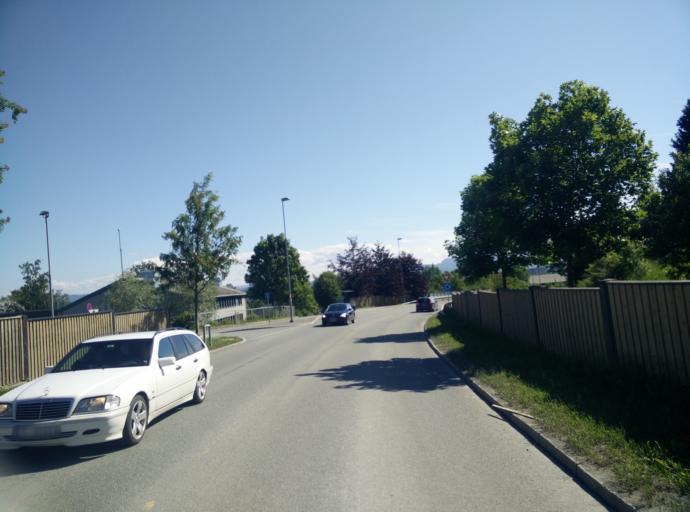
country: NO
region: Sor-Trondelag
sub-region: Trondheim
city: Trondheim
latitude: 63.3999
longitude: 10.3581
